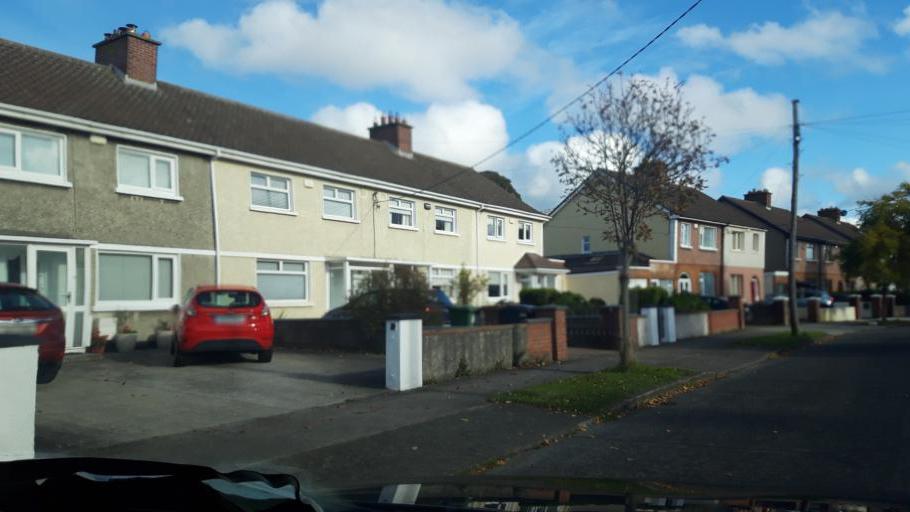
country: IE
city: Coolock
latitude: 53.3872
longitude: -6.2058
